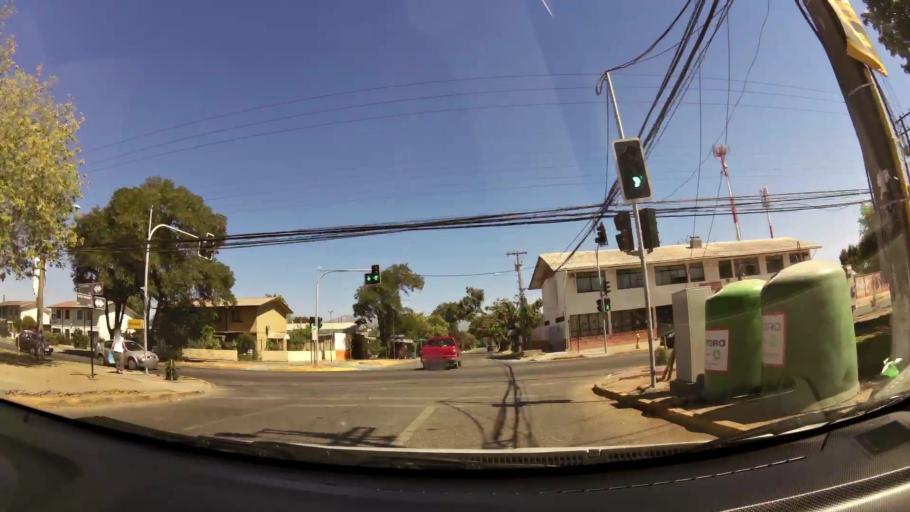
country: CL
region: O'Higgins
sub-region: Provincia de Cachapoal
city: Rancagua
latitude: -34.1764
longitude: -70.7205
